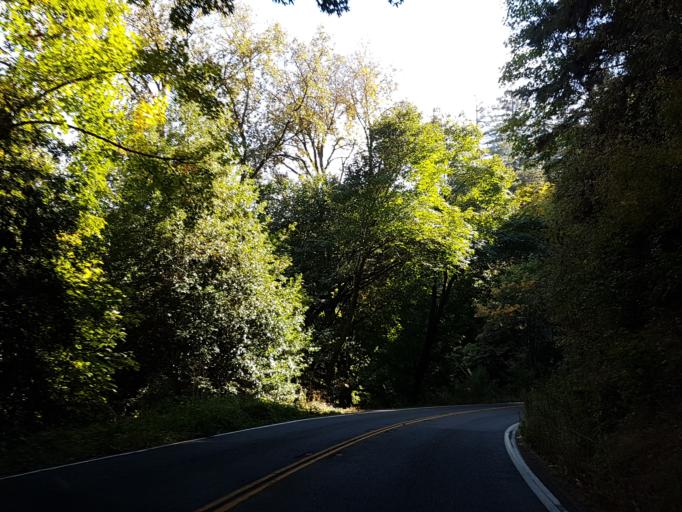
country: US
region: California
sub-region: Humboldt County
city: Rio Dell
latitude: 40.4211
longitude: -123.9779
